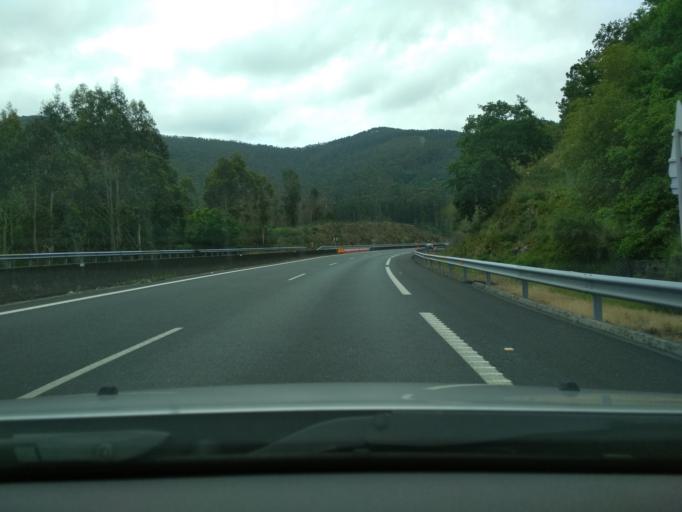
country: ES
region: Galicia
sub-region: Provincia da Coruna
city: Padron
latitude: 42.8004
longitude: -8.6240
